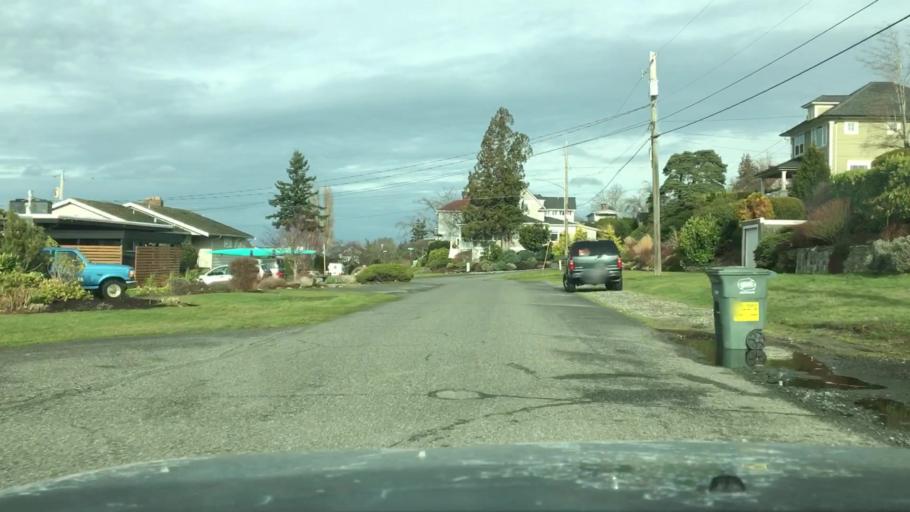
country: US
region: Washington
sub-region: Whatcom County
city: Bellingham
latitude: 48.7232
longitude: -122.5011
